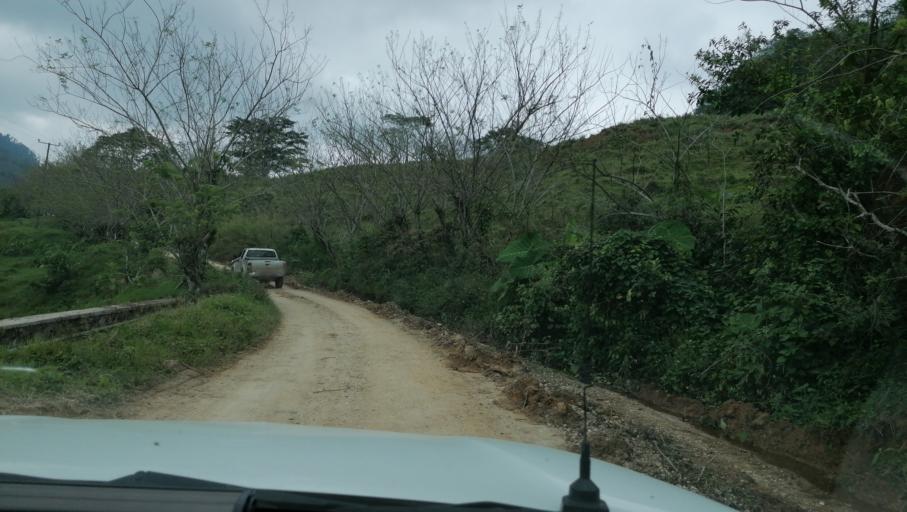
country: MX
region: Chiapas
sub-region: Ocotepec
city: San Pablo Huacano
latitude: 17.2680
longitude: -93.2556
